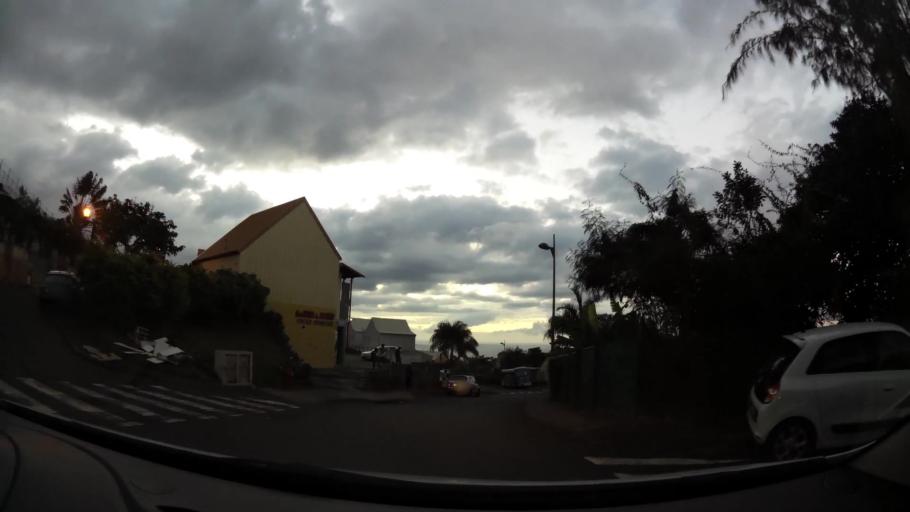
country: RE
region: Reunion
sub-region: Reunion
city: Saint-Denis
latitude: -20.9098
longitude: 55.4653
